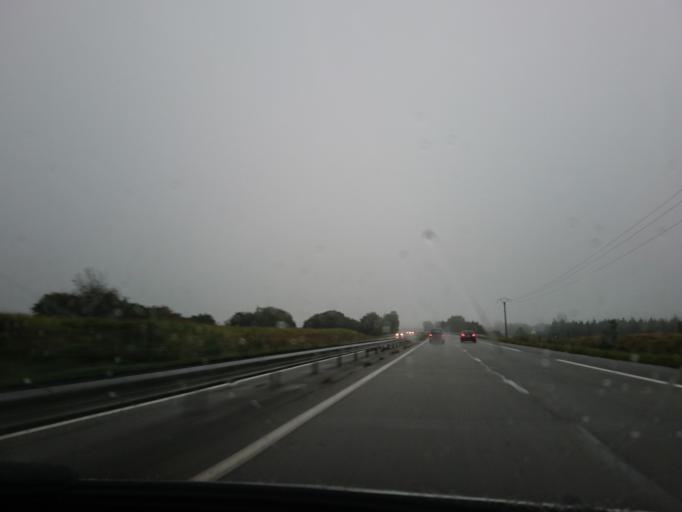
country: FR
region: Brittany
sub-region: Departement du Finistere
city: Landrevarzec
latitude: 48.0900
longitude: -4.0382
